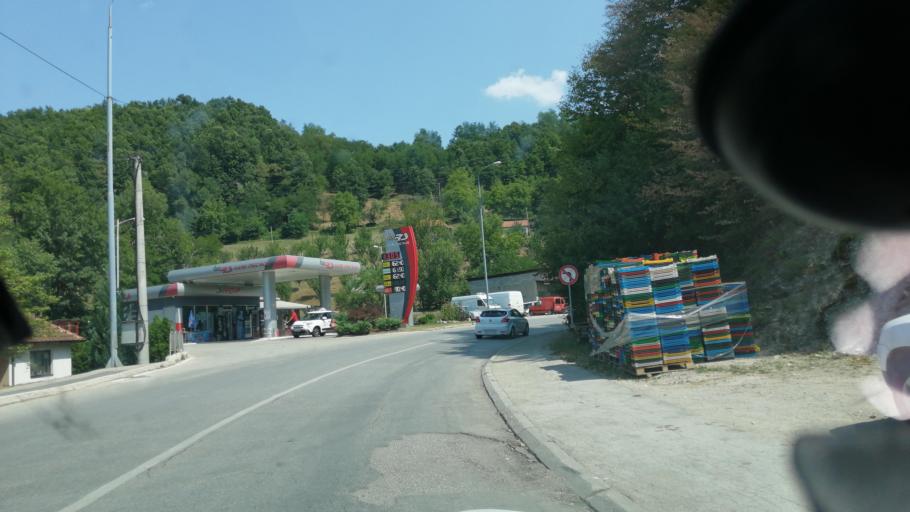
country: RS
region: Central Serbia
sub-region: Moravicki Okrug
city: Ivanjica
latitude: 43.5996
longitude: 20.2241
